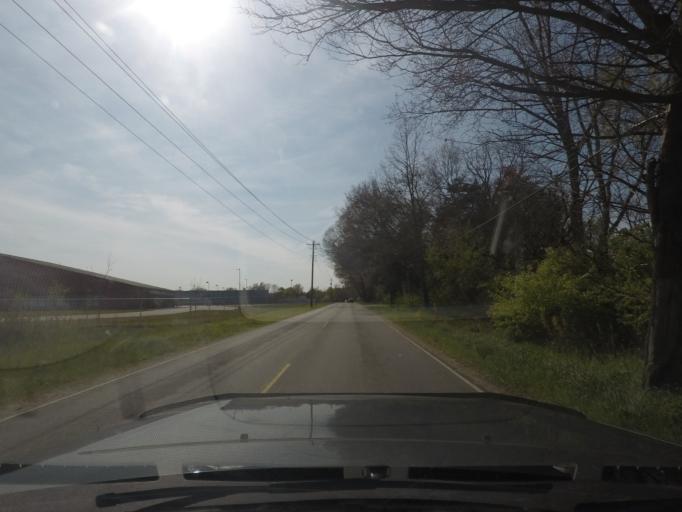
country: US
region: Indiana
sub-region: Elkhart County
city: Elkhart
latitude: 41.7045
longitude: -86.0083
